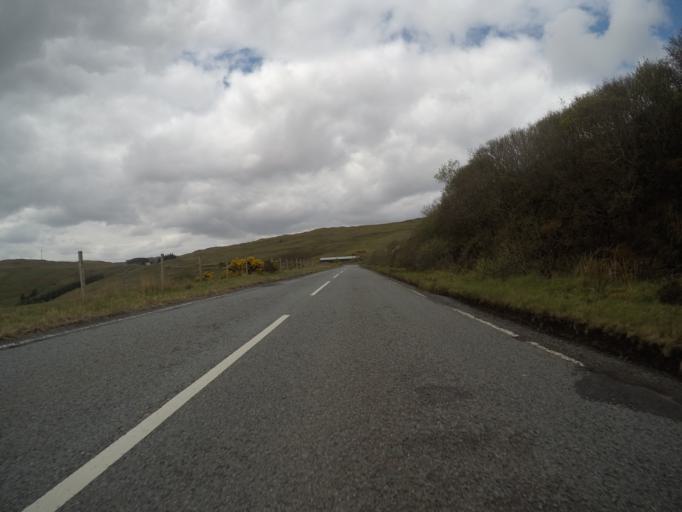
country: GB
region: Scotland
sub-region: Highland
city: Isle of Skye
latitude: 57.3268
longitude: -6.3333
